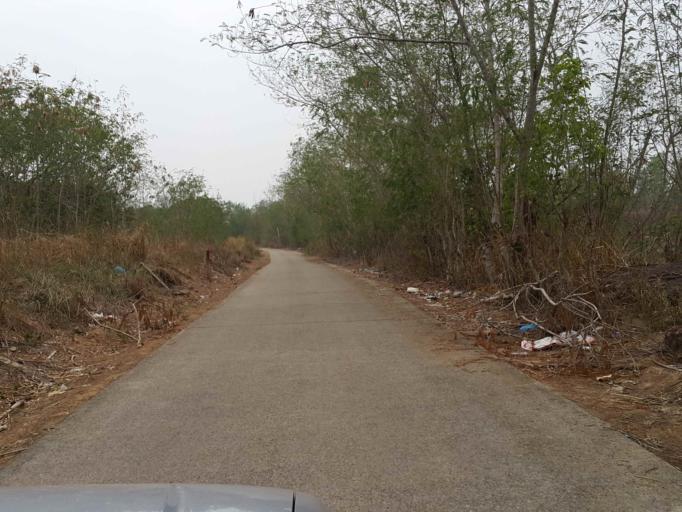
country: TH
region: Chiang Mai
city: San Sai
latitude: 18.9448
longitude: 99.0155
